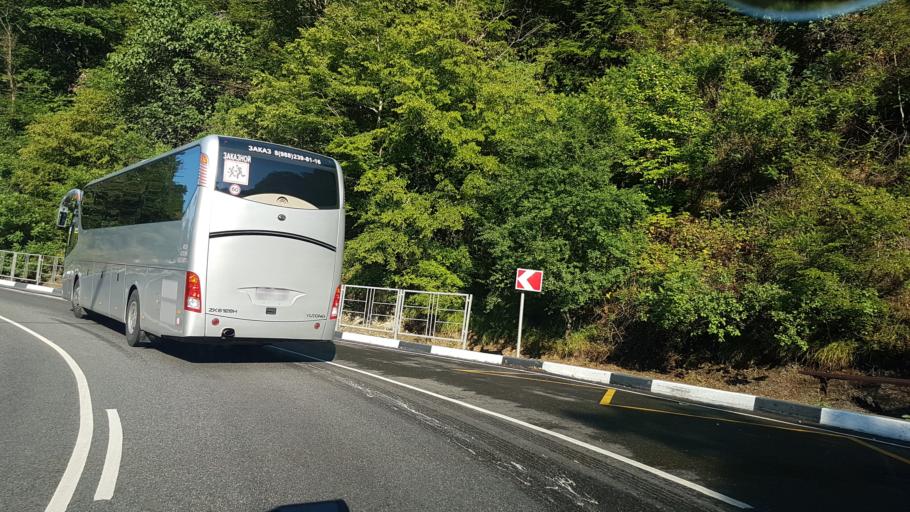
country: RU
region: Krasnodarskiy
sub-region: Sochi City
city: Lazarevskoye
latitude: 43.8441
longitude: 39.4168
